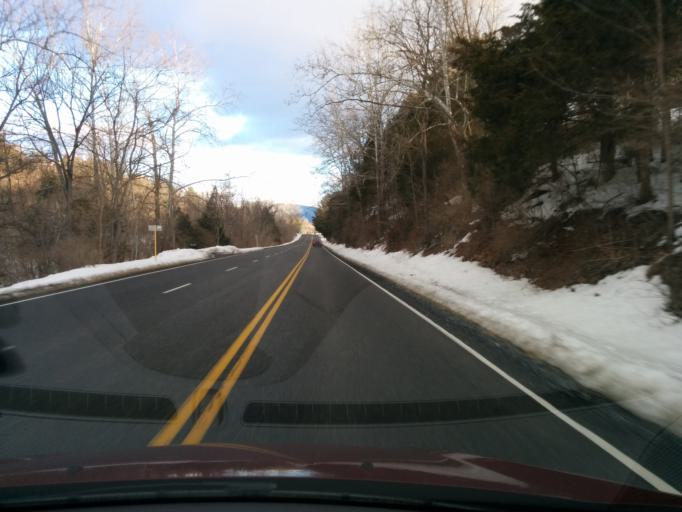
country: US
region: Virginia
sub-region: City of Lexington
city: Lexington
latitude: 37.7643
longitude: -79.4468
